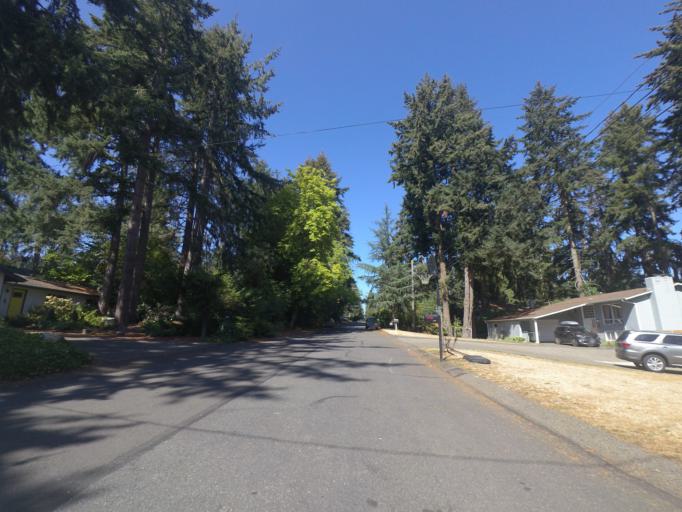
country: US
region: Washington
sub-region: Pierce County
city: Fircrest
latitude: 47.2200
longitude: -122.5149
